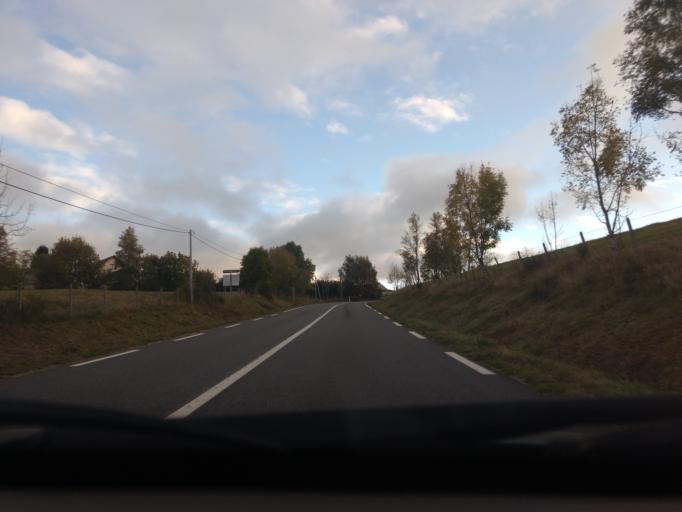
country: FR
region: Midi-Pyrenees
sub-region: Departement de l'Aveyron
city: Laguiole
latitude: 44.6762
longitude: 2.8512
